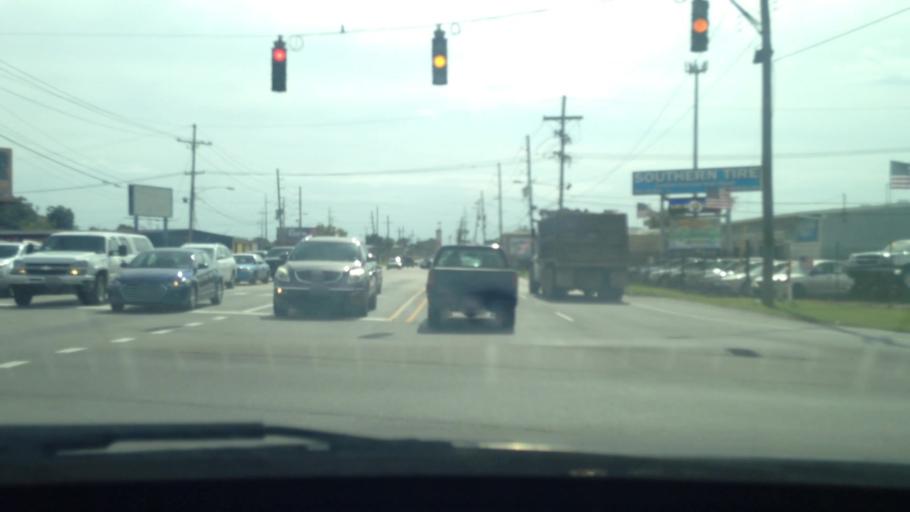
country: US
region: Louisiana
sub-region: Jefferson Parish
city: River Ridge
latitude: 29.9778
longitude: -90.2109
